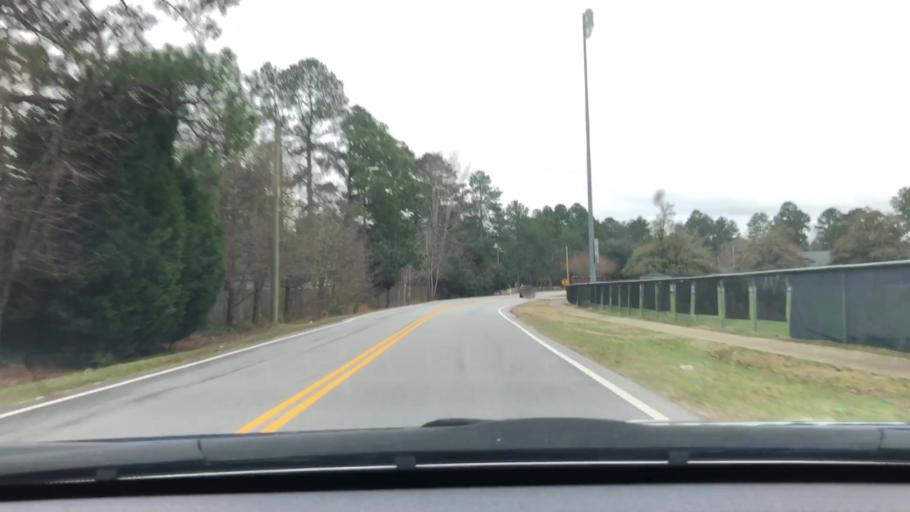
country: US
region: South Carolina
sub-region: Sumter County
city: Cherryvale
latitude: 33.9372
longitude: -80.4045
